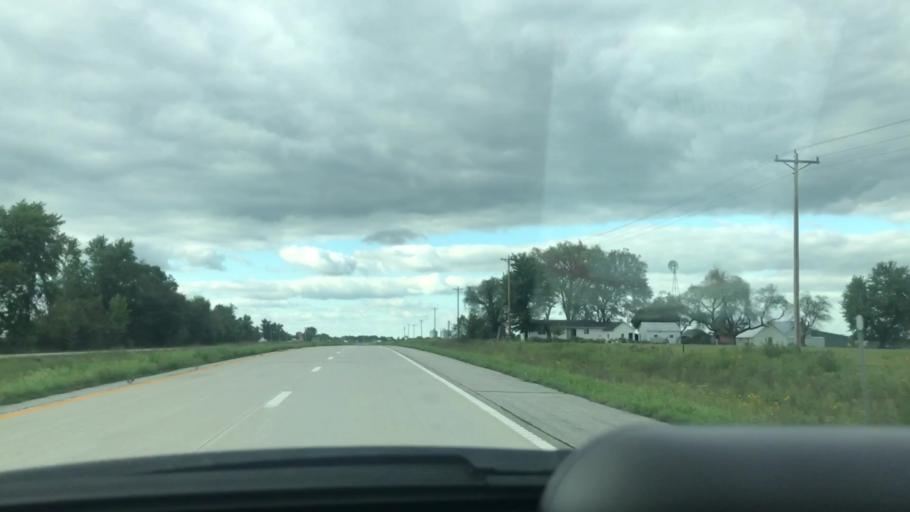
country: US
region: Missouri
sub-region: Benton County
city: Lincoln
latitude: 38.3680
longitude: -93.3388
